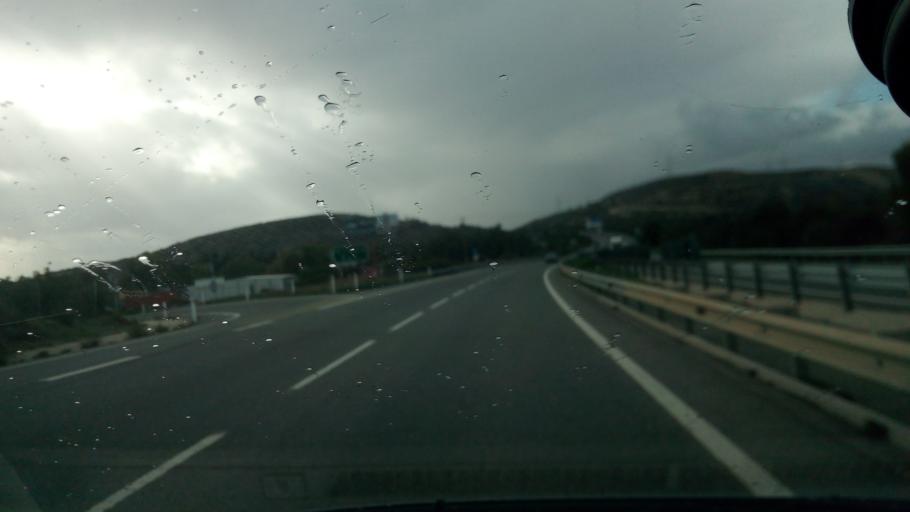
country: CY
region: Limassol
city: Pyrgos
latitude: 34.7219
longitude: 33.2018
